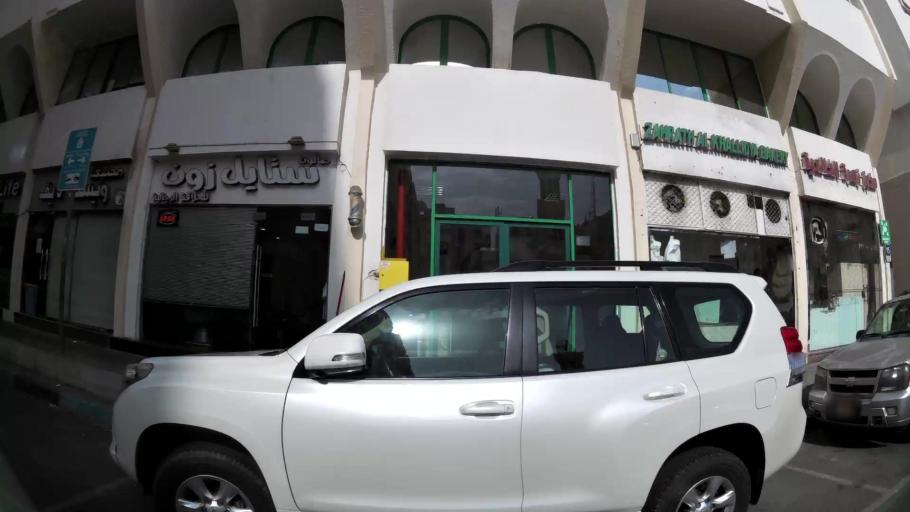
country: AE
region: Abu Dhabi
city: Abu Dhabi
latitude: 24.4709
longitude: 54.3476
